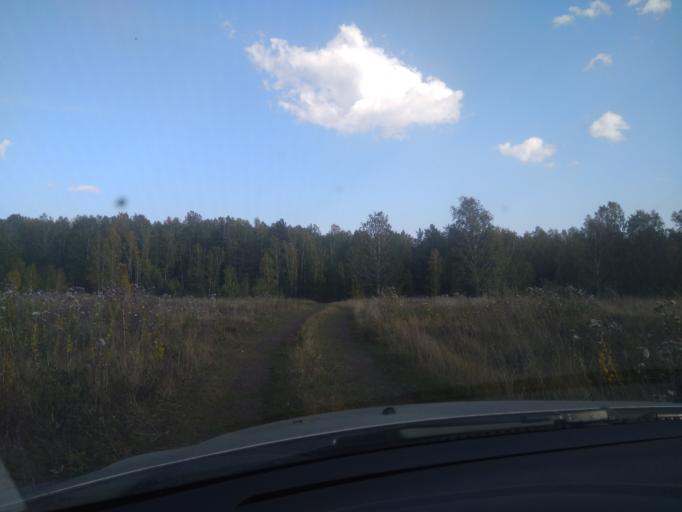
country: RU
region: Sverdlovsk
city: Pokrovskoye
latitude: 56.4266
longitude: 61.6139
